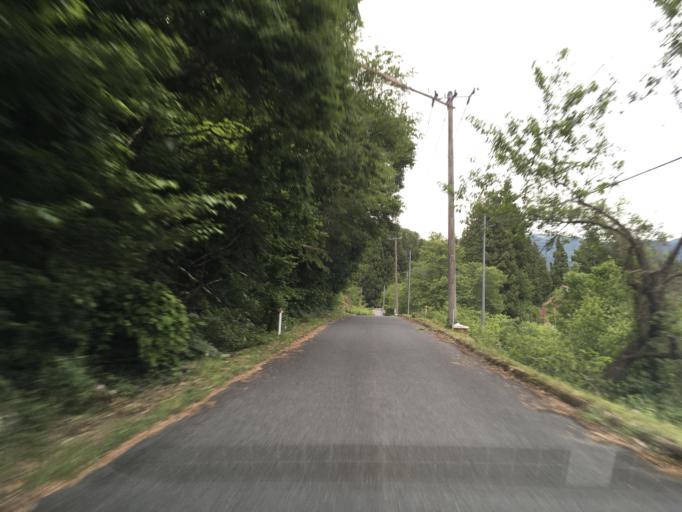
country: JP
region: Iwate
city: Mizusawa
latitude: 39.1575
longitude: 141.2937
